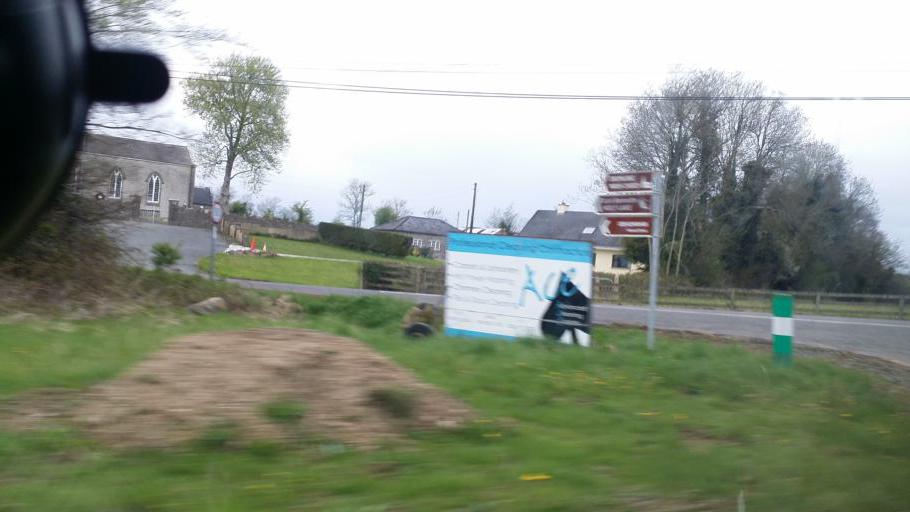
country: IE
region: Ulster
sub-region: An Cabhan
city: Belturbet
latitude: 54.0898
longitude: -7.4997
